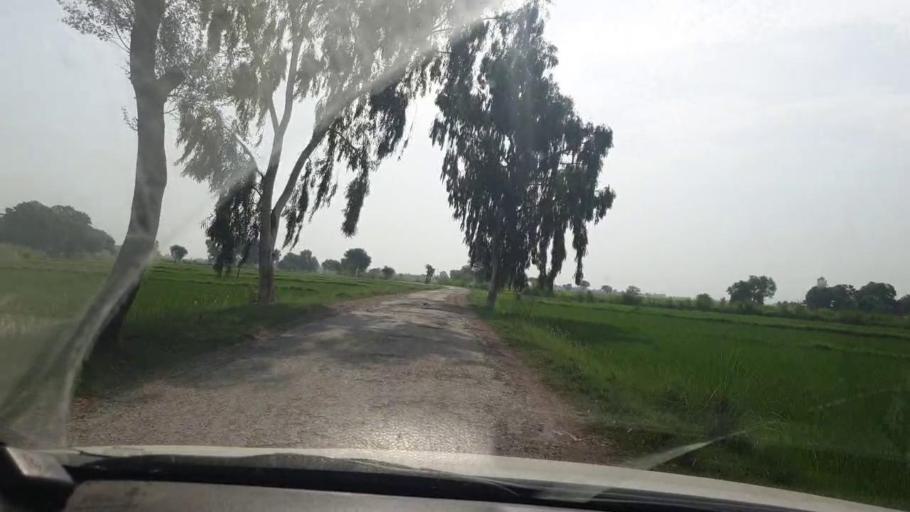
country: PK
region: Sindh
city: Lakhi
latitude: 27.8296
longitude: 68.7456
